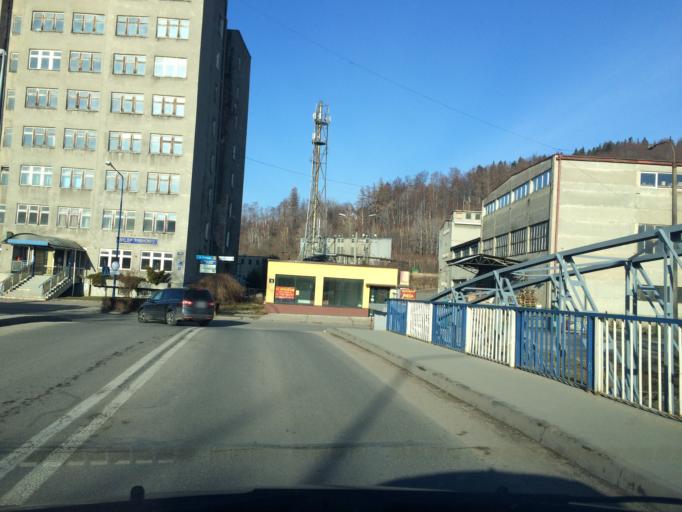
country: PL
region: Lower Silesian Voivodeship
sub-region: Powiat klodzki
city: Stronie Slaskie
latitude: 50.2990
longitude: 16.8763
